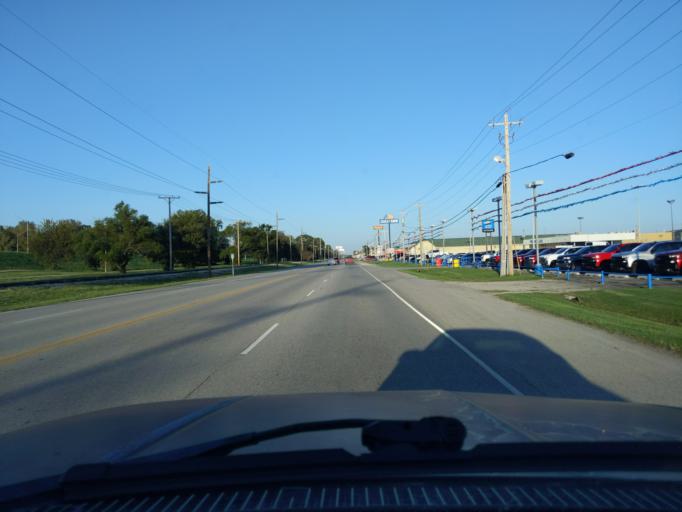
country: US
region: Oklahoma
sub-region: Tulsa County
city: Sand Springs
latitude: 36.1385
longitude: -96.0951
